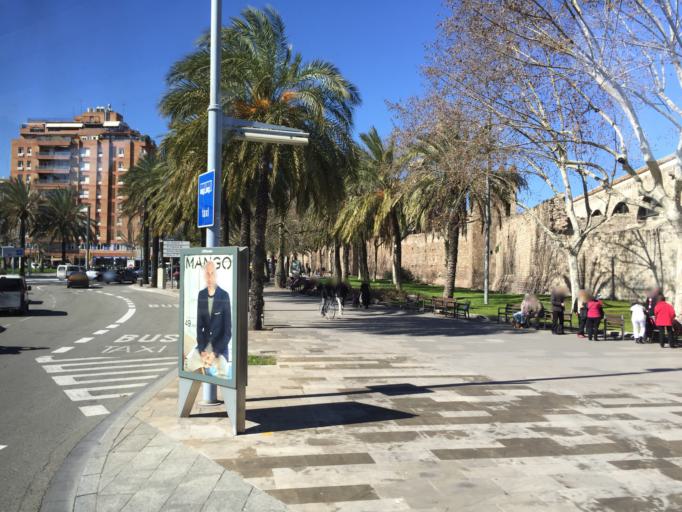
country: ES
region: Catalonia
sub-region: Provincia de Barcelona
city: Ciutat Vella
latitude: 41.3745
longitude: 2.1766
